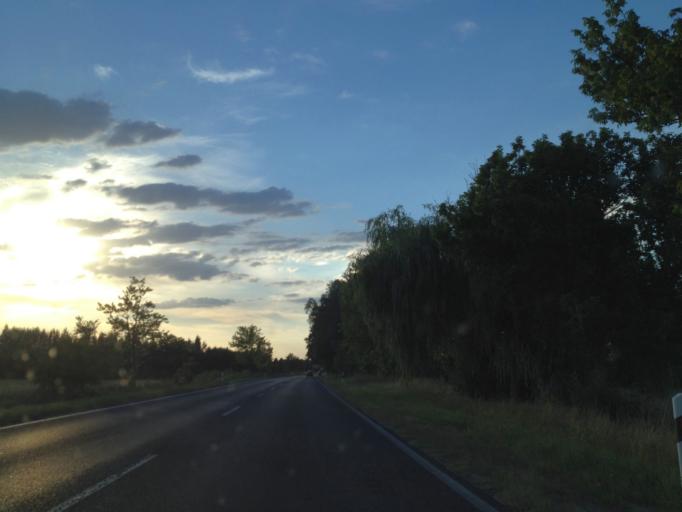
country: HU
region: Gyor-Moson-Sopron
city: Otteveny
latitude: 47.7165
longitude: 17.5098
